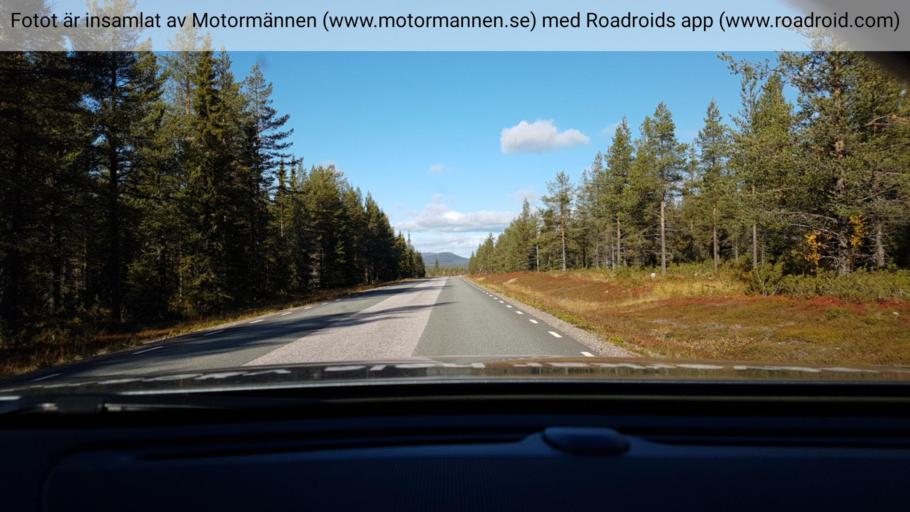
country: SE
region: Norrbotten
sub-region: Arjeplogs Kommun
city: Arjeplog
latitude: 65.8117
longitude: 18.4536
